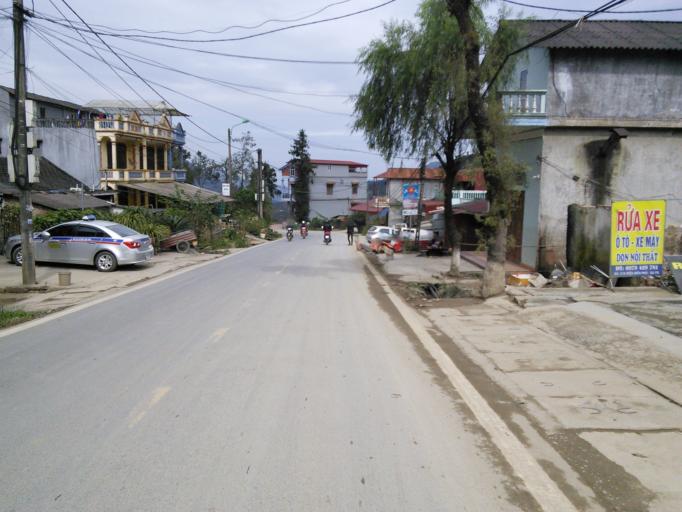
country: VN
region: Lao Cai
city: Sa Pa
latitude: 22.3431
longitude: 103.8571
